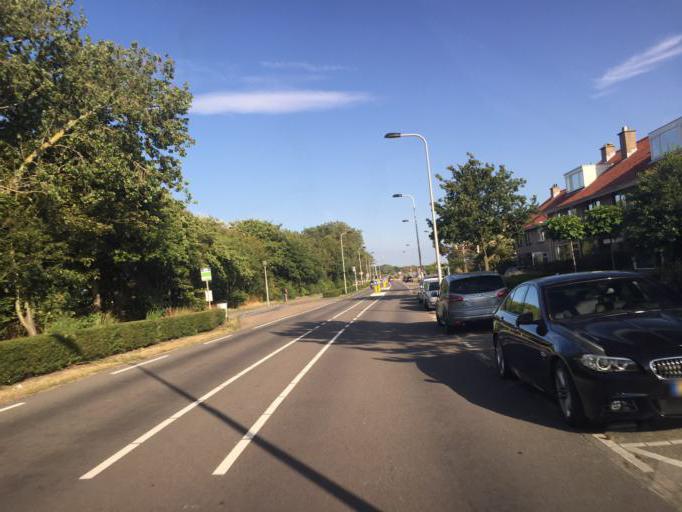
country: NL
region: South Holland
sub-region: Gemeente Noordwijk
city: Noordwijk-Binnen
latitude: 52.2509
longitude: 4.4461
